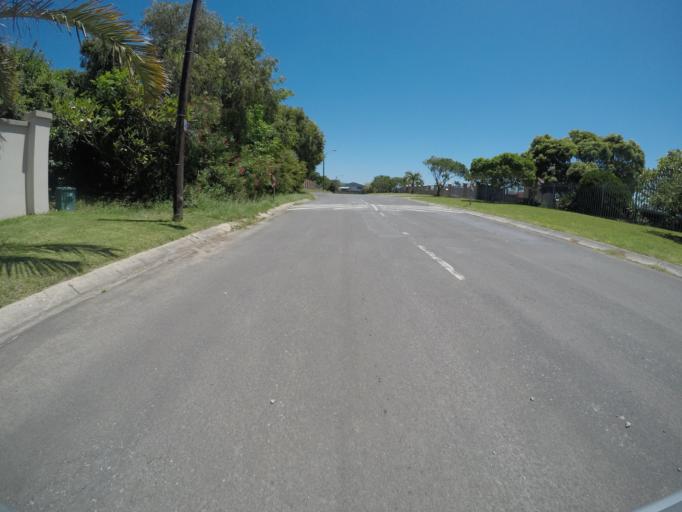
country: ZA
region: Eastern Cape
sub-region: Buffalo City Metropolitan Municipality
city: East London
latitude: -32.9562
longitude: 27.9391
